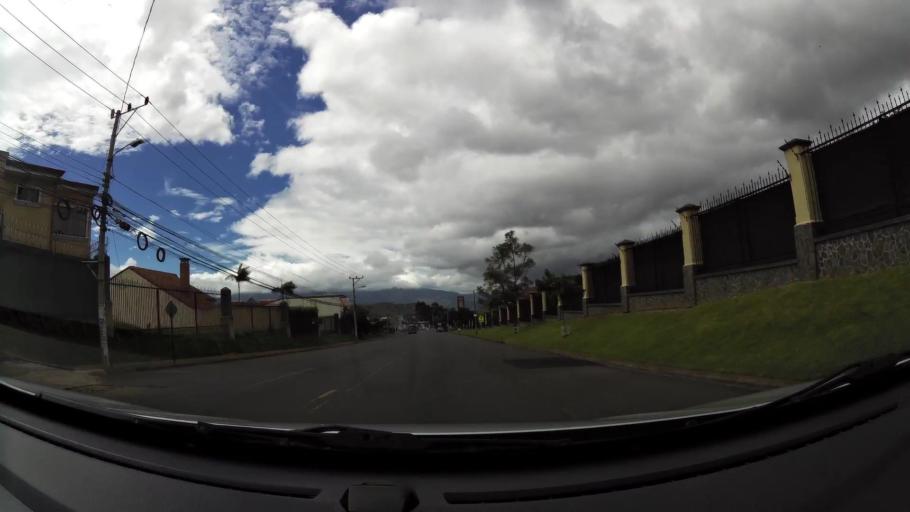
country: CR
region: Cartago
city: San Diego
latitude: 9.9090
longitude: -84.0051
